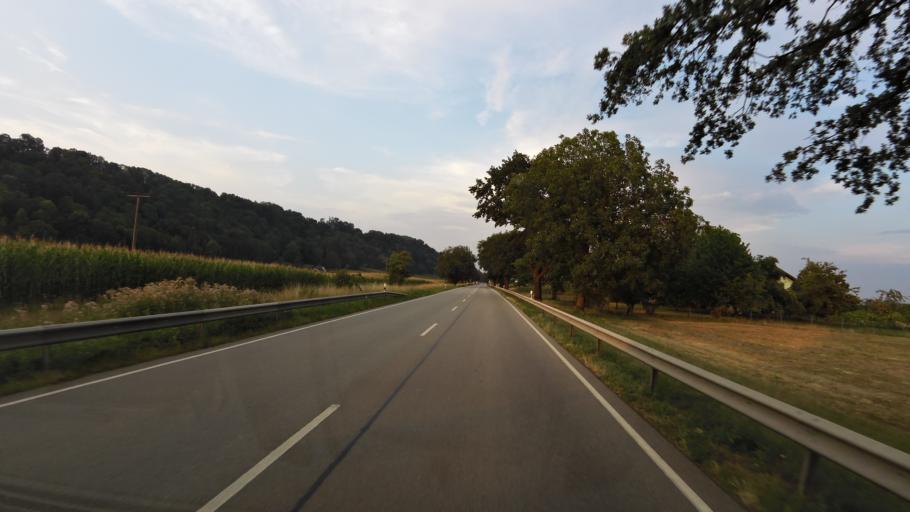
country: DE
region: Bavaria
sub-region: Lower Bavaria
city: Ering
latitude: 48.3059
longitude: 13.1560
